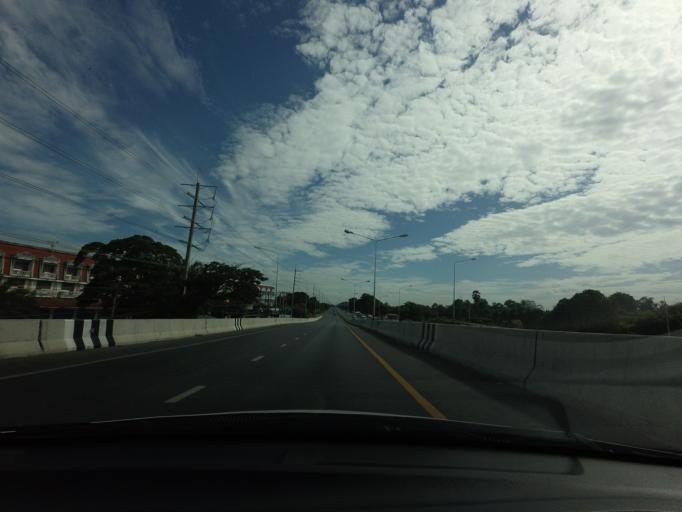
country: TH
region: Pathum Thani
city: Nong Suea
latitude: 14.0777
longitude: 100.8953
